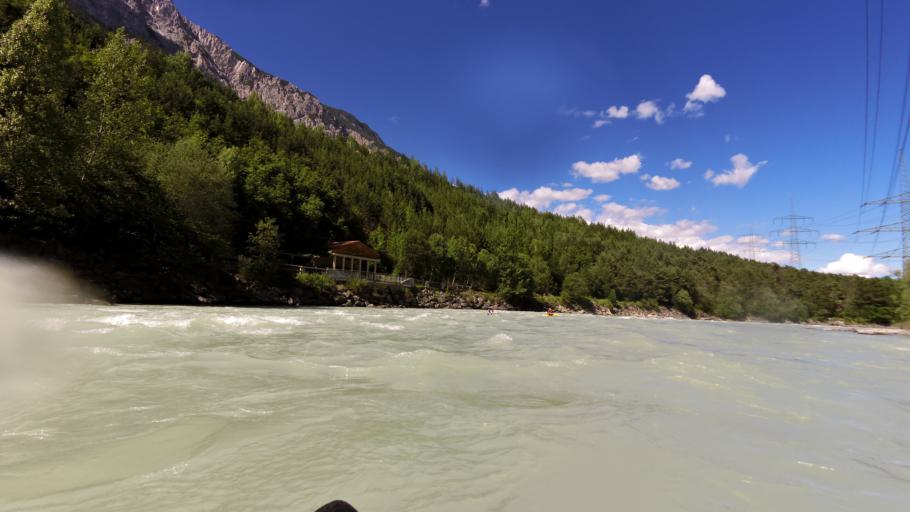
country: AT
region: Tyrol
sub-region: Politischer Bezirk Imst
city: Roppen
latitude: 47.2267
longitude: 10.8207
